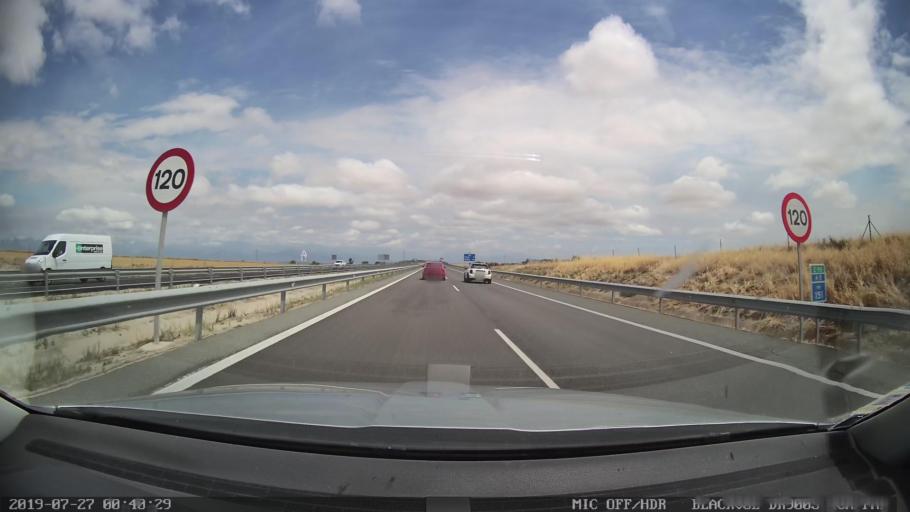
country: ES
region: Castille-La Mancha
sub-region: Province of Toledo
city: Lagartera
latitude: 39.9133
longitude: -5.2096
